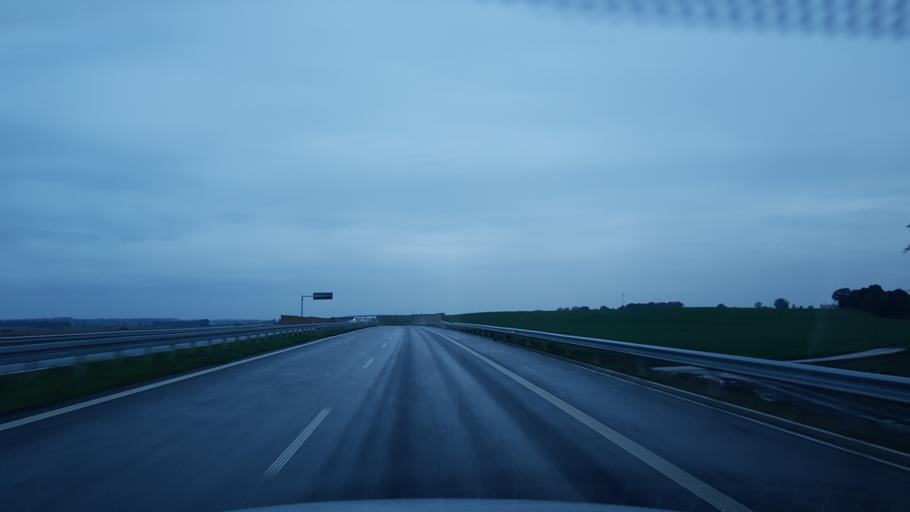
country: PL
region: West Pomeranian Voivodeship
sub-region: Powiat gryficki
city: Brojce
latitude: 53.9676
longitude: 15.4244
